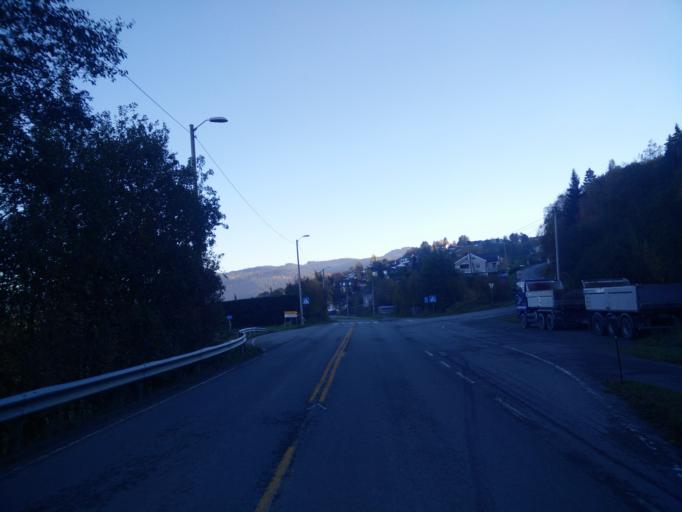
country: NO
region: Sor-Trondelag
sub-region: Skaun
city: Borsa
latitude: 63.3380
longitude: 10.0593
